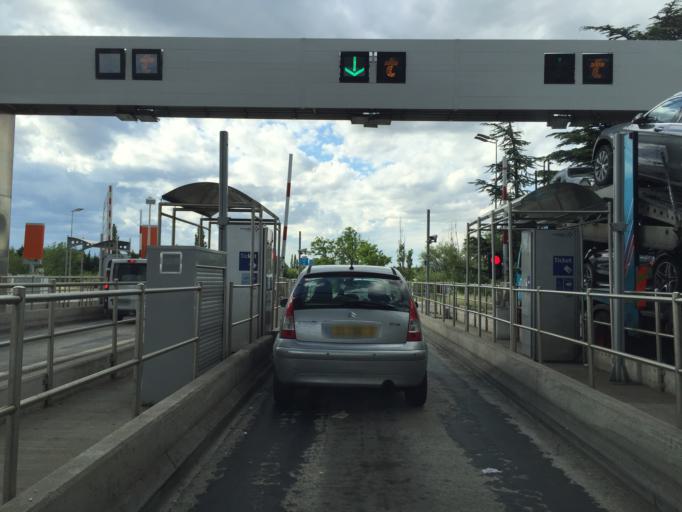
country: FR
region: Provence-Alpes-Cote d'Azur
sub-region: Departement des Bouches-du-Rhone
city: Noves
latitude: 43.8929
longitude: 4.9160
